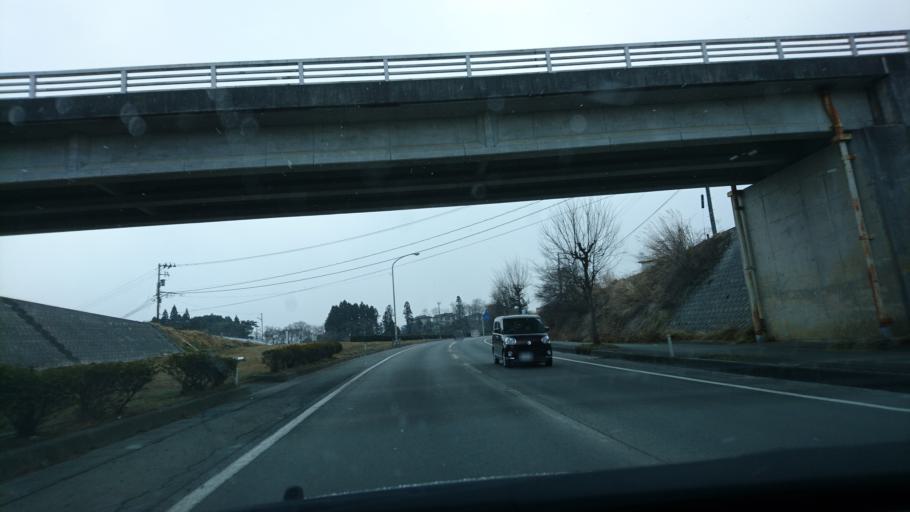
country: JP
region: Iwate
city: Ofunato
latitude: 38.8845
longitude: 141.5667
